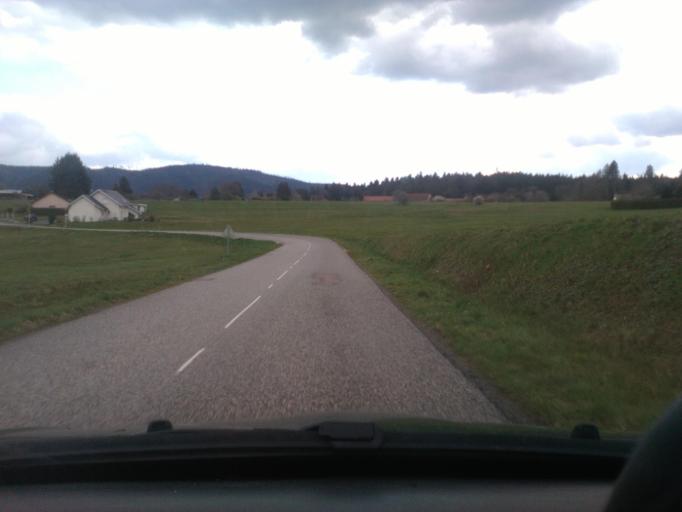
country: FR
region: Lorraine
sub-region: Departement des Vosges
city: Etival-Clairefontaine
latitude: 48.3283
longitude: 6.8256
